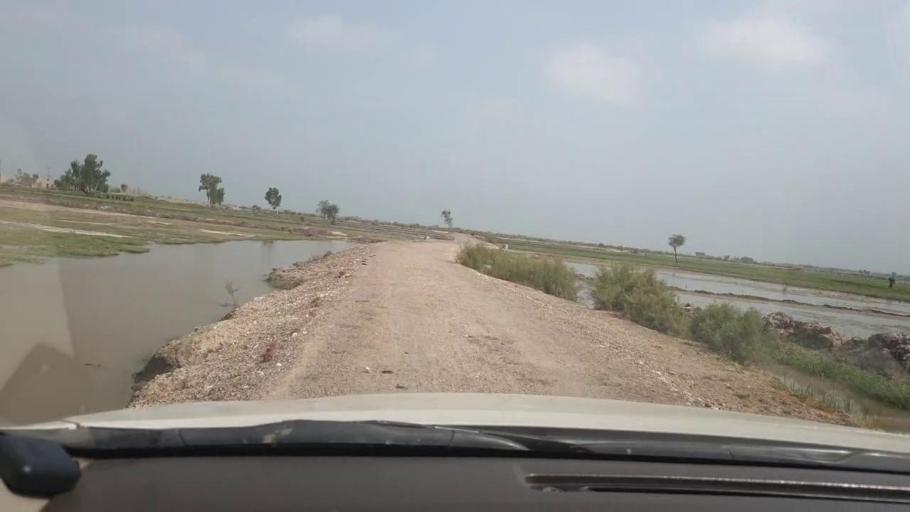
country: PK
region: Sindh
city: Shikarpur
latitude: 28.0225
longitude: 68.5901
